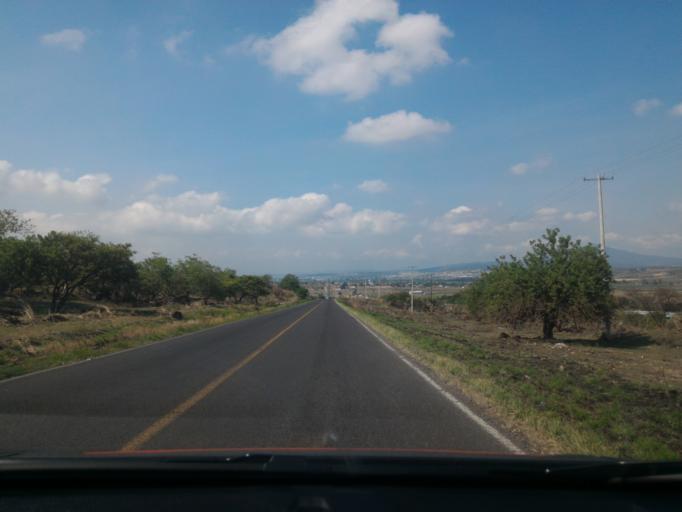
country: MX
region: Guanajuato
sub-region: Penjamo
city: Estacion la Piedad
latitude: 20.4290
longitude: -101.9910
